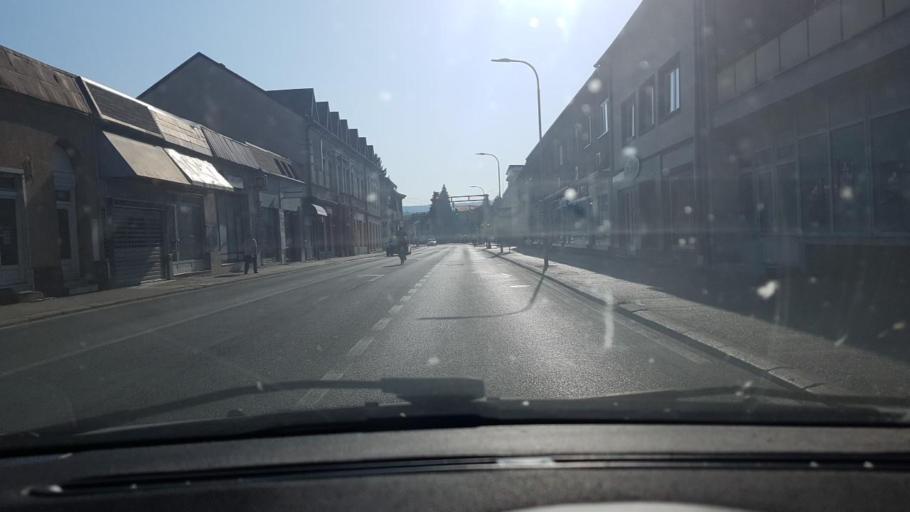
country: BA
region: Federation of Bosnia and Herzegovina
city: Bihac
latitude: 44.8139
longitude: 15.8734
